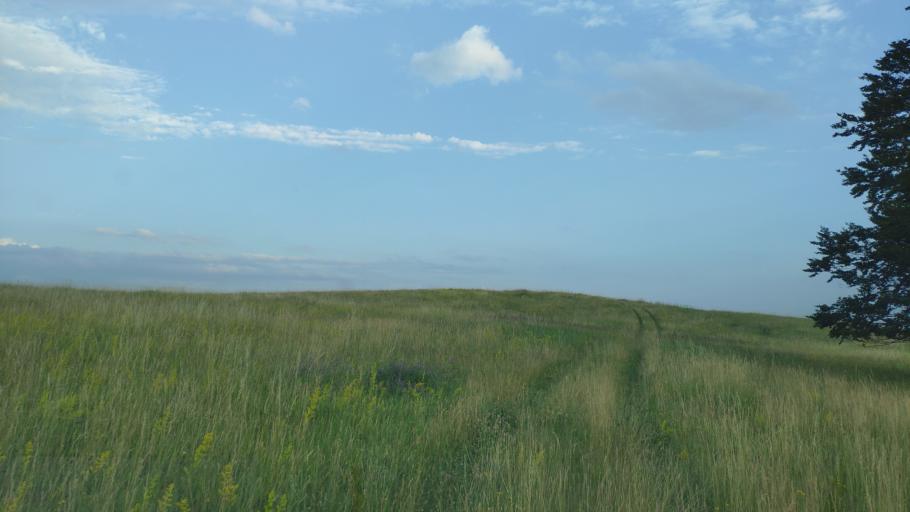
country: SK
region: Kosicky
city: Moldava nad Bodvou
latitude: 48.7150
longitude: 21.0013
